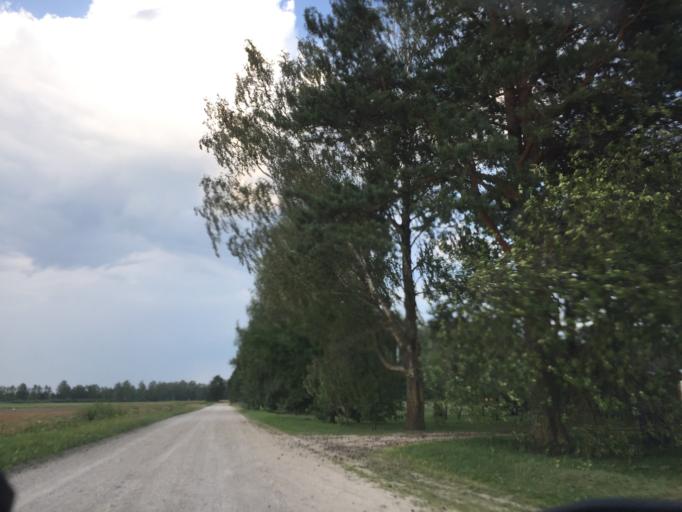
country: LV
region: Dobeles Rajons
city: Dobele
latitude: 56.6156
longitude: 23.3567
